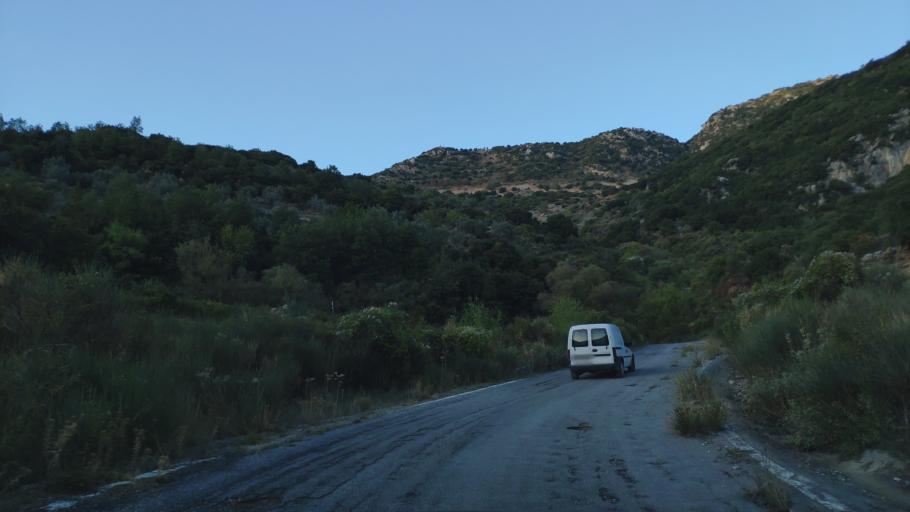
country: GR
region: Peloponnese
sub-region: Nomos Arkadias
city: Dimitsana
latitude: 37.5760
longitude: 22.0515
